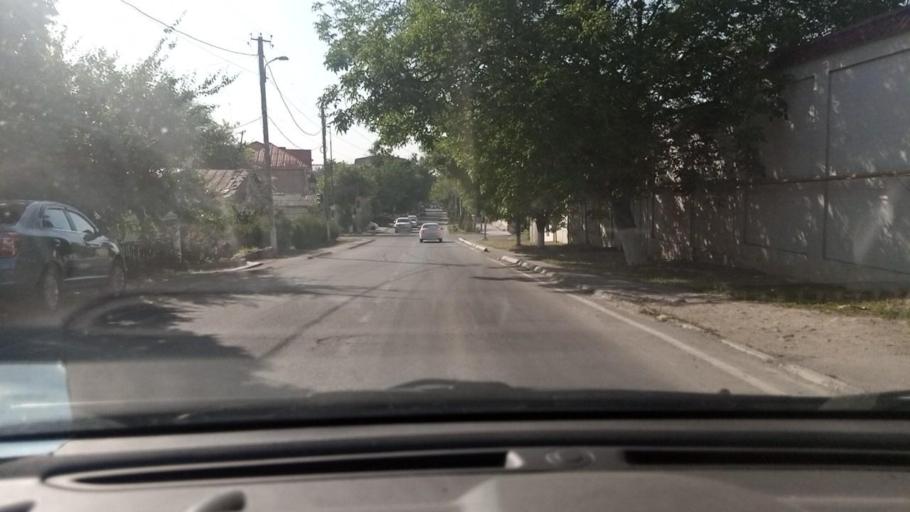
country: UZ
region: Toshkent
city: Salor
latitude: 41.3394
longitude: 69.3526
